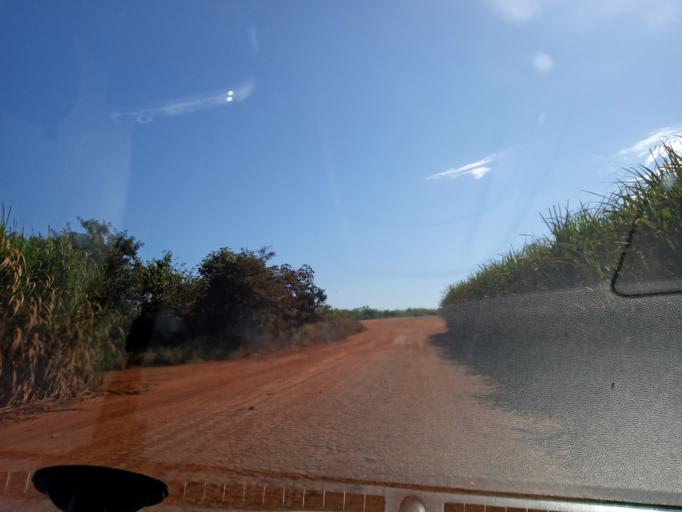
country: BR
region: Goias
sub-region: Itumbiara
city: Itumbiara
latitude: -18.4452
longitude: -49.1754
